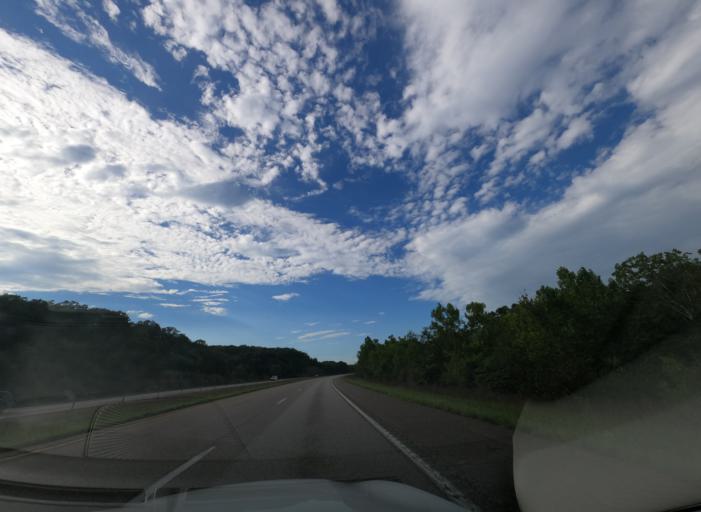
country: US
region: Missouri
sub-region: Jefferson County
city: Crystal City
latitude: 38.0714
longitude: -90.2913
